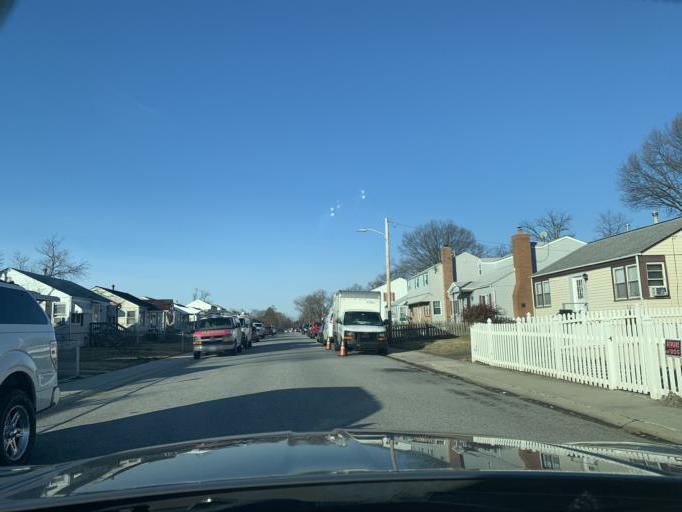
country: US
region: Maryland
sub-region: Anne Arundel County
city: Glen Burnie
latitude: 39.1534
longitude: -76.6238
